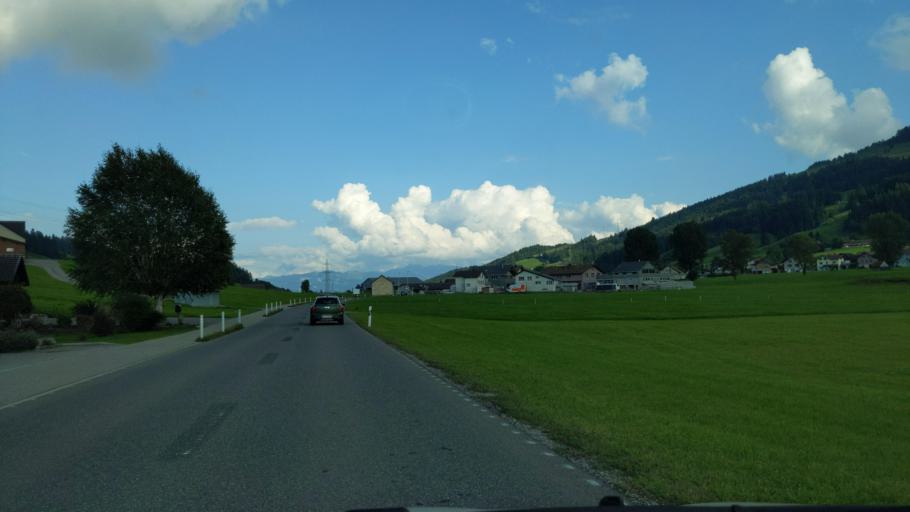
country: CH
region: Appenzell Ausserrhoden
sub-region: Bezirk Mittelland
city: Gais
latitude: 47.3344
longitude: 9.4583
